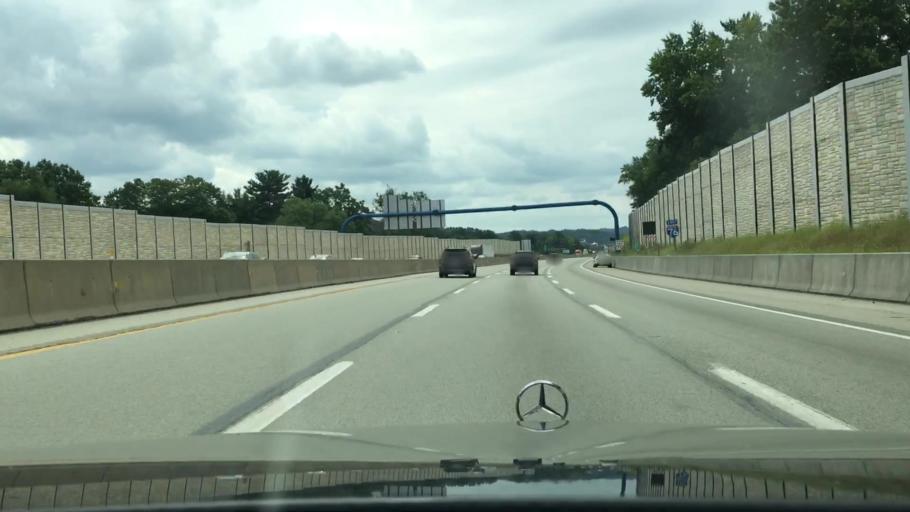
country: US
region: Pennsylvania
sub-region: Westmoreland County
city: Manor
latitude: 40.3047
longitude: -79.6733
